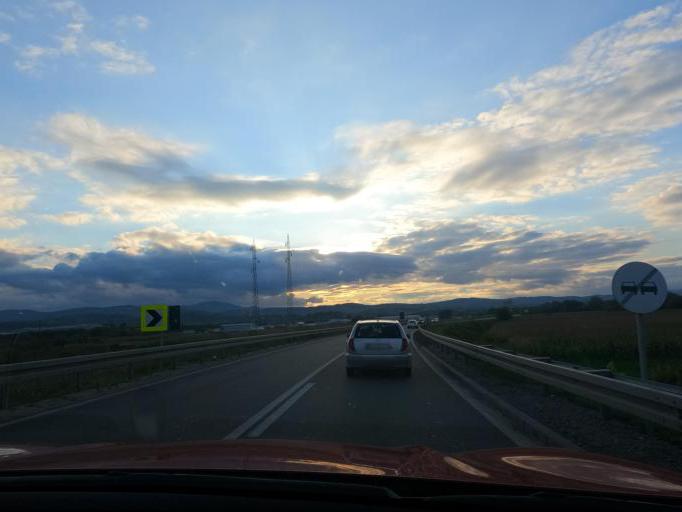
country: RS
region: Central Serbia
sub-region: Zlatiborski Okrug
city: Pozega
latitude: 43.8370
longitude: 20.0494
